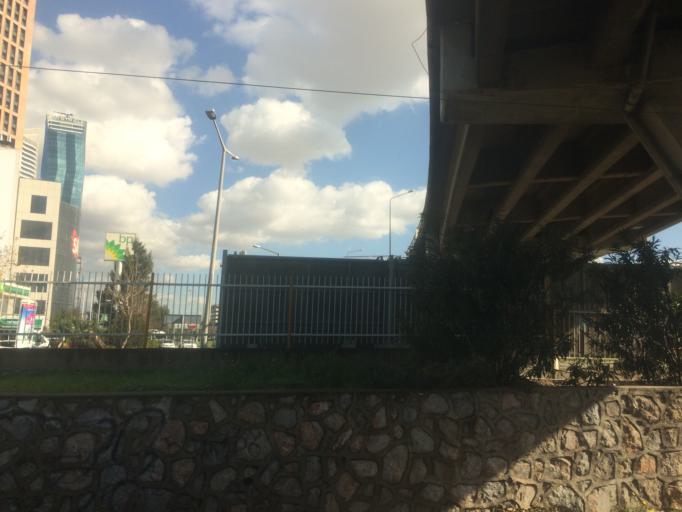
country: TR
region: Izmir
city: Buca
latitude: 38.4461
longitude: 27.1733
